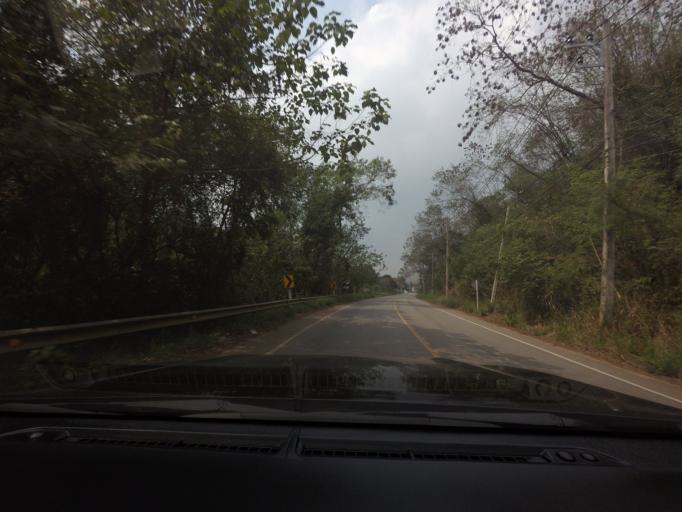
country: TH
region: Sara Buri
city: Muak Lek
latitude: 14.5402
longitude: 101.3420
